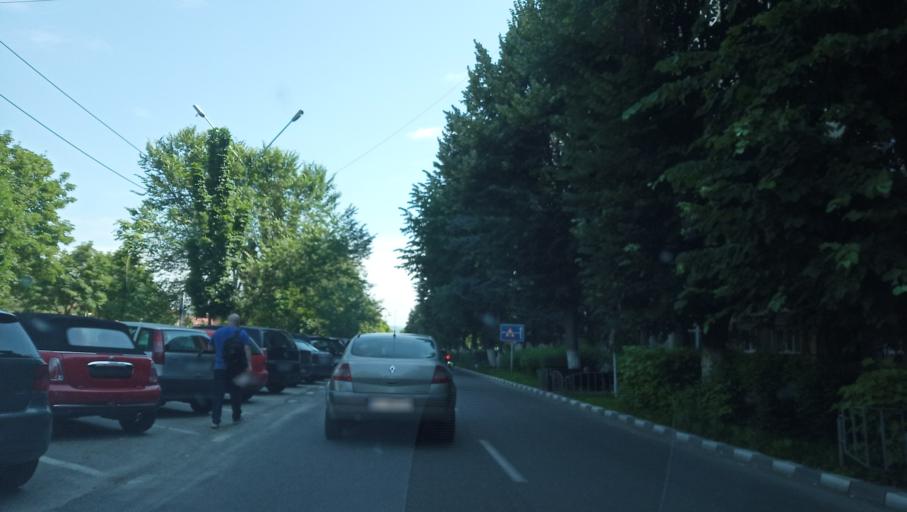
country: RO
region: Valcea
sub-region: Municipiul Ramnicu Valcea
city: Ramnicu Valcea
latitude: 45.0936
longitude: 24.3652
